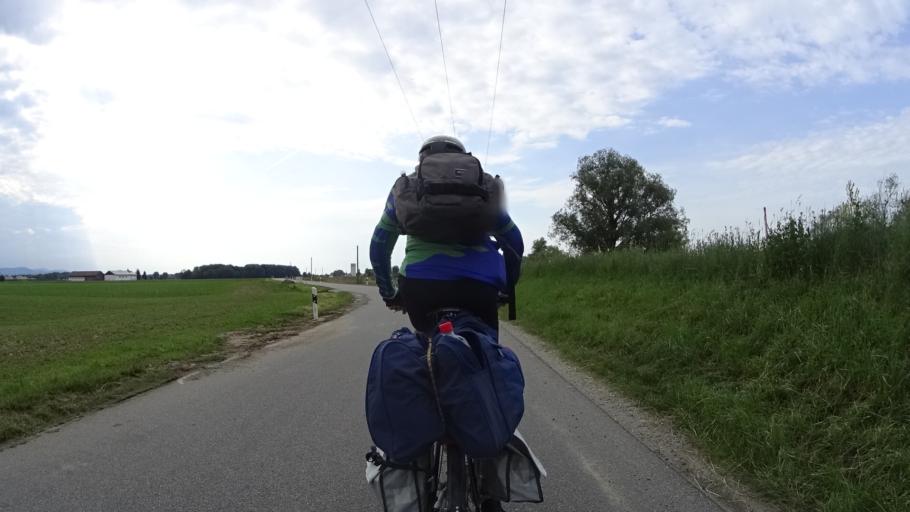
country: DE
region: Bavaria
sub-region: Lower Bavaria
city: Irlbach
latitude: 48.8693
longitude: 12.7587
